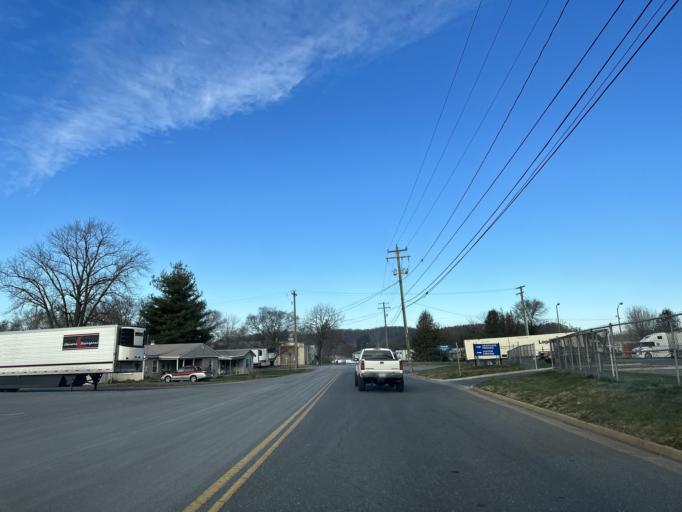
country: US
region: Virginia
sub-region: Rockingham County
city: Bridgewater
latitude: 38.3909
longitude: -78.9674
